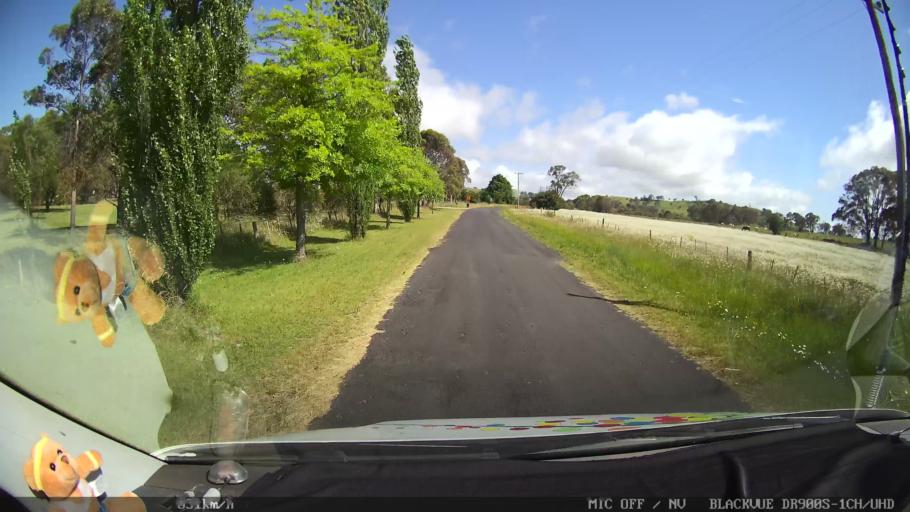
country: AU
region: New South Wales
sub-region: Guyra
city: Guyra
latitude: -30.0176
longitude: 151.6580
